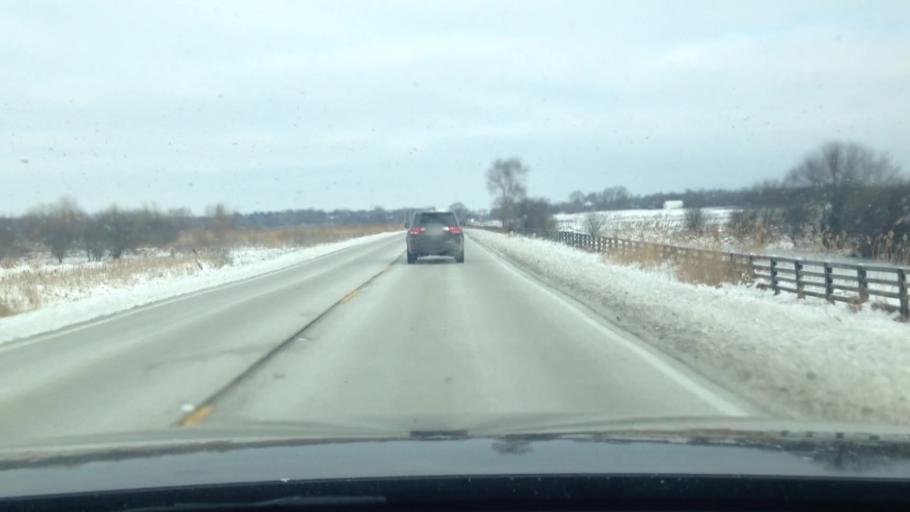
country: US
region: Illinois
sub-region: McHenry County
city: Huntley
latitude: 42.2181
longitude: -88.4224
